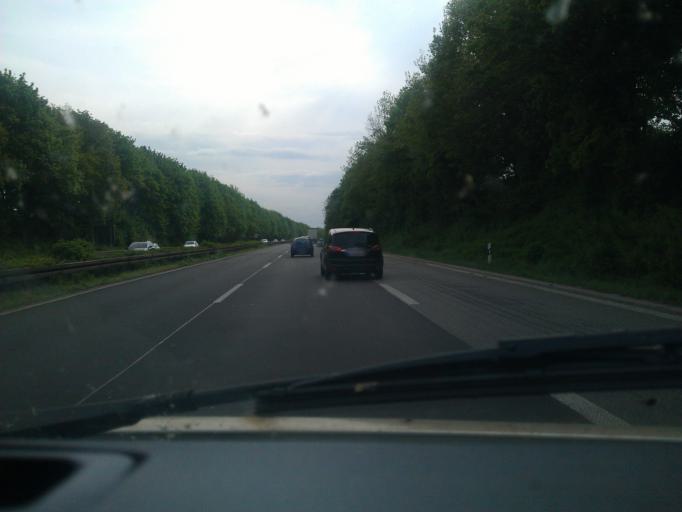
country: DE
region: North Rhine-Westphalia
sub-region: Regierungsbezirk Koln
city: Aldenhoven
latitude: 50.9108
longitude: 6.3174
